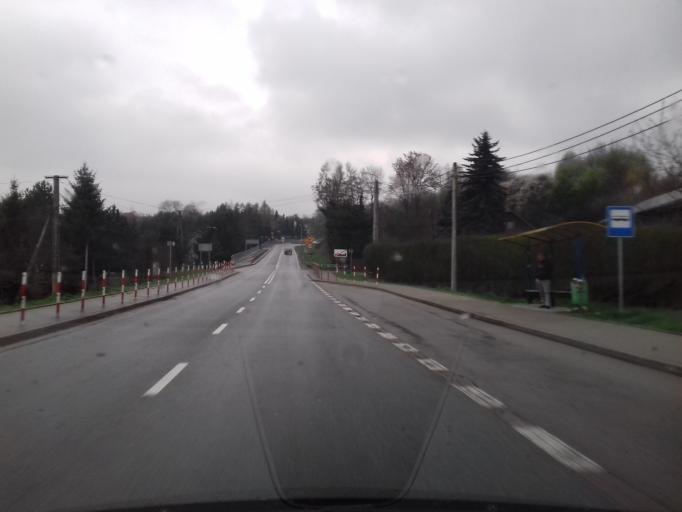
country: PL
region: Lesser Poland Voivodeship
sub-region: Powiat nowosadecki
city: Chelmiec
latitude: 49.6312
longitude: 20.6455
